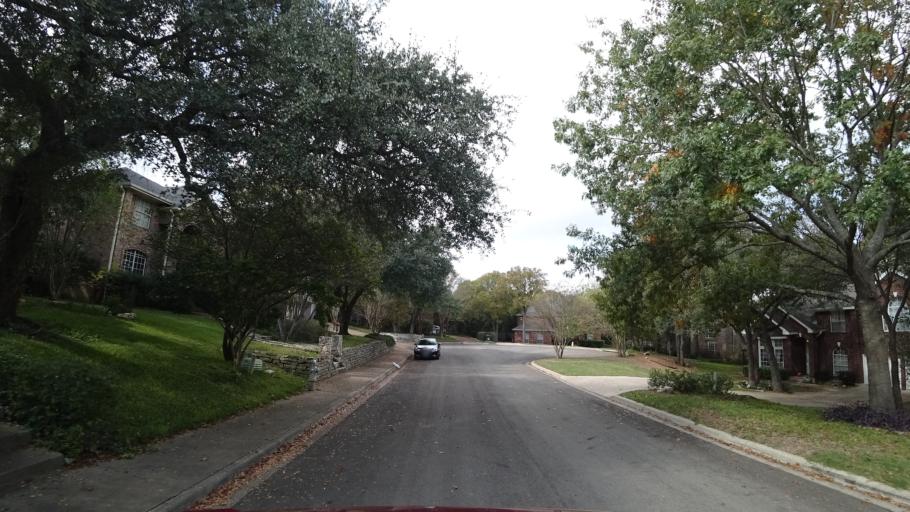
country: US
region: Texas
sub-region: Williamson County
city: Anderson Mill
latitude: 30.4203
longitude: -97.8580
